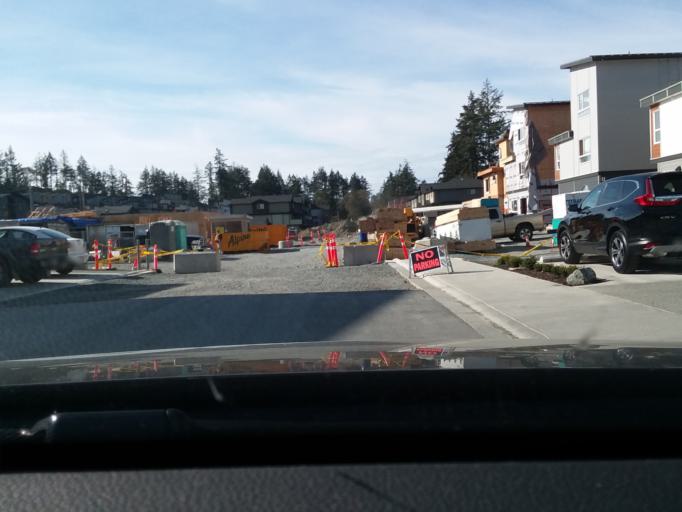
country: CA
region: British Columbia
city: Langford
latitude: 48.4277
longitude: -123.5309
